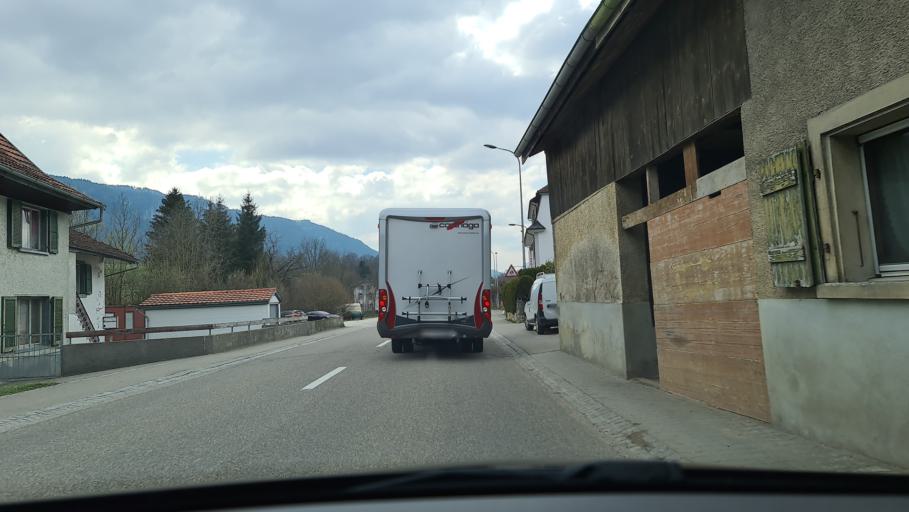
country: CH
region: Bern
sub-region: Jura bernois
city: Moutier
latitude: 47.2834
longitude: 7.4245
